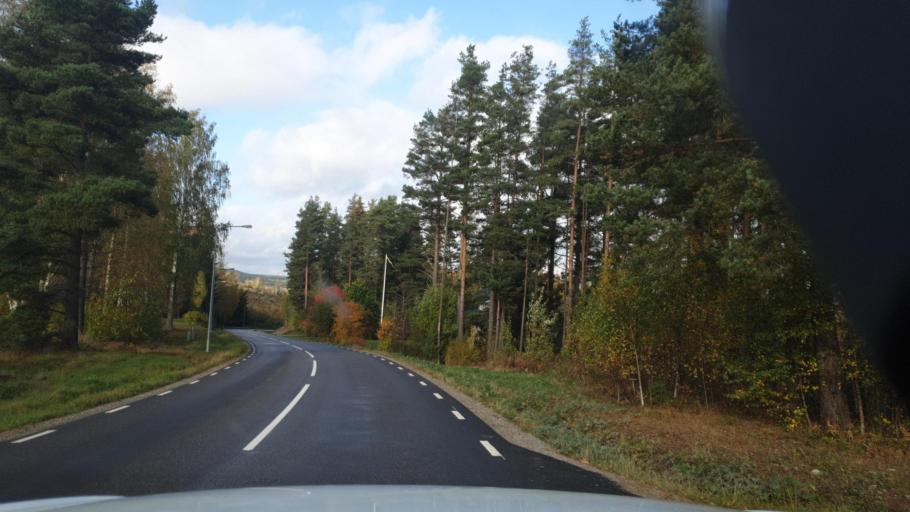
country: SE
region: Vaermland
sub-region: Arvika Kommun
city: Arvika
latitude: 59.5436
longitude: 12.5773
